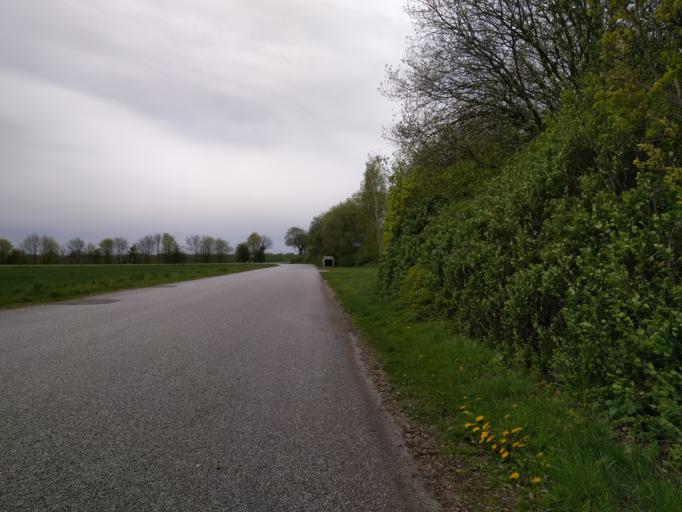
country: DK
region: South Denmark
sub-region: Kerteminde Kommune
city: Munkebo
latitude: 55.4661
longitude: 10.5916
